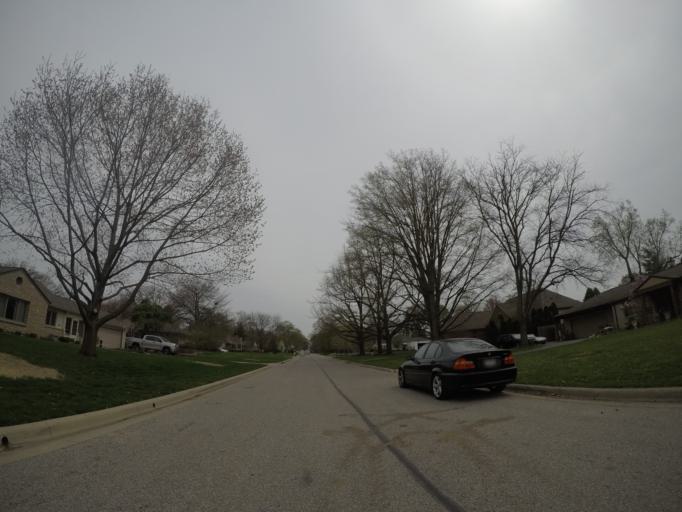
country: US
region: Ohio
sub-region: Franklin County
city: Upper Arlington
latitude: 40.0139
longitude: -83.0811
